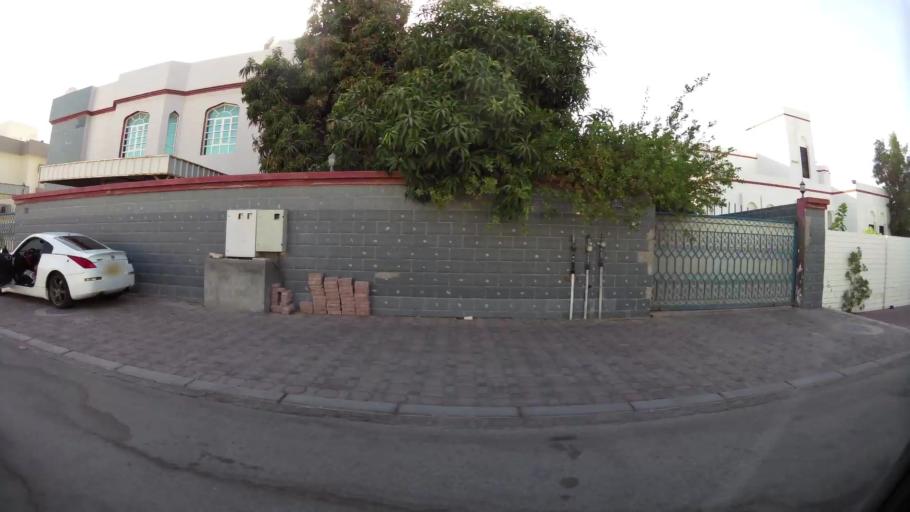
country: OM
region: Muhafazat Masqat
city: As Sib al Jadidah
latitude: 23.6359
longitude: 58.2035
